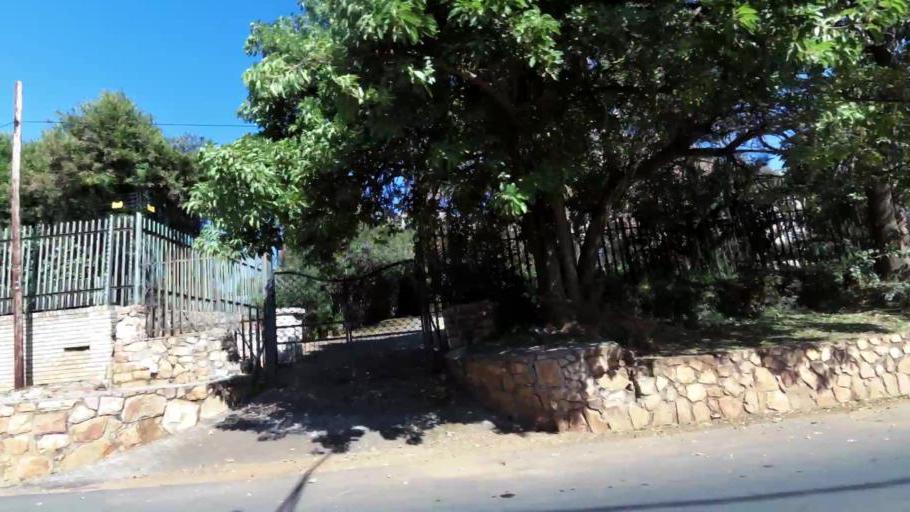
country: ZA
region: Gauteng
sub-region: City of Johannesburg Metropolitan Municipality
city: Johannesburg
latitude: -26.1421
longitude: 27.9739
